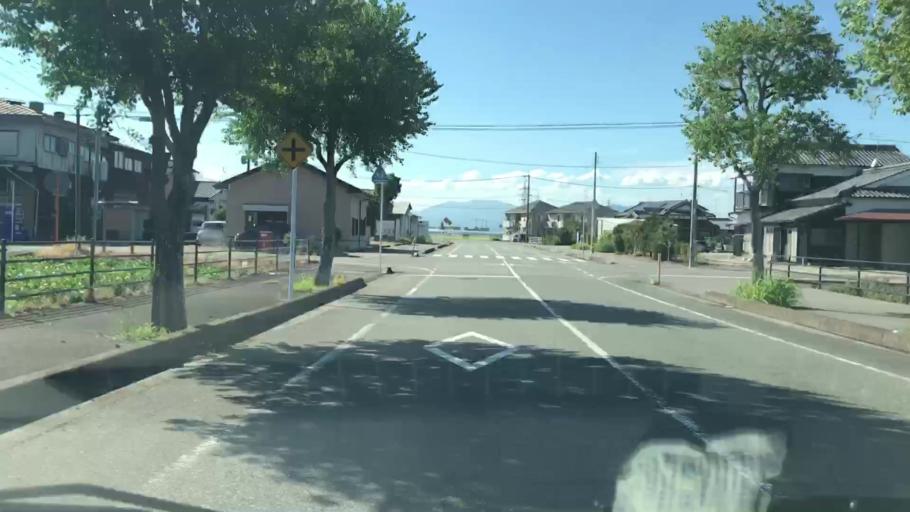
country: JP
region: Saga Prefecture
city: Okawa
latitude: 33.2296
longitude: 130.3681
